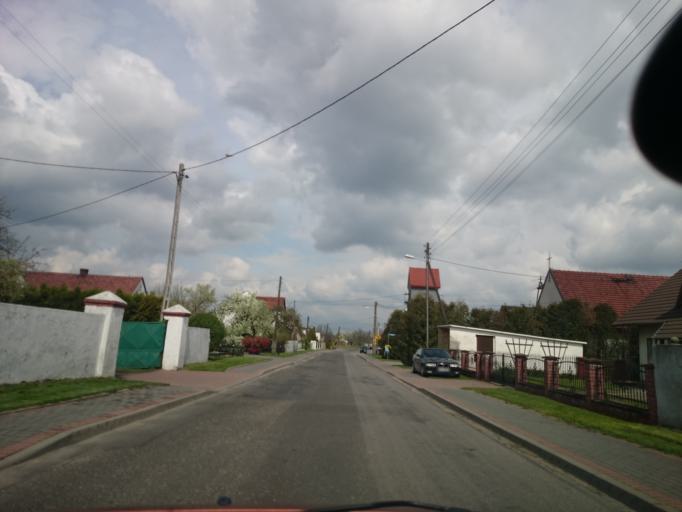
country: PL
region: Opole Voivodeship
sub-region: Powiat opolski
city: Naklo
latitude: 50.5150
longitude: 18.1223
